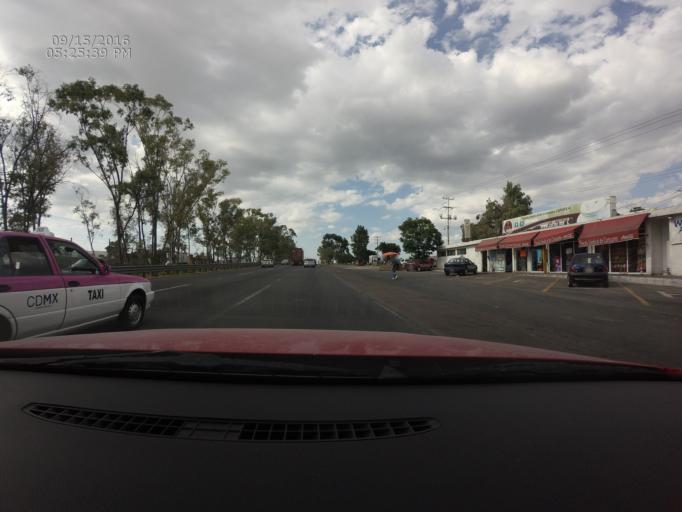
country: MX
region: Mexico
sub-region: Cuautitlan
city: San Jose del Puente
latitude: 19.7309
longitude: -99.2101
